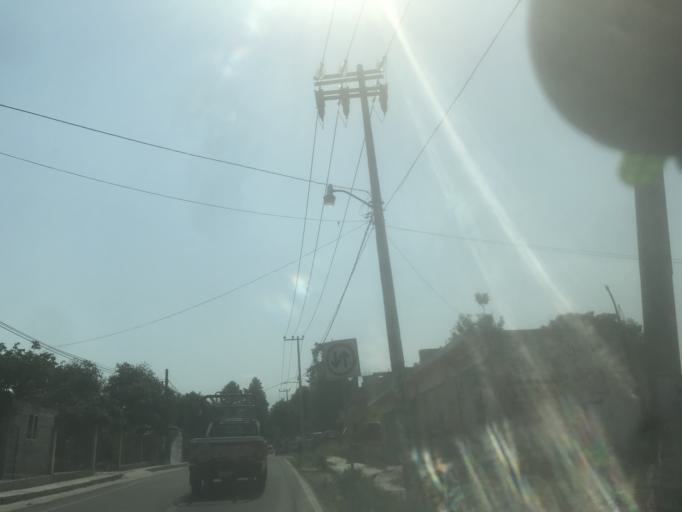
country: MX
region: Mexico
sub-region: Atlautla
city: San Juan Tepecoculco
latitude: 18.9913
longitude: -98.7917
